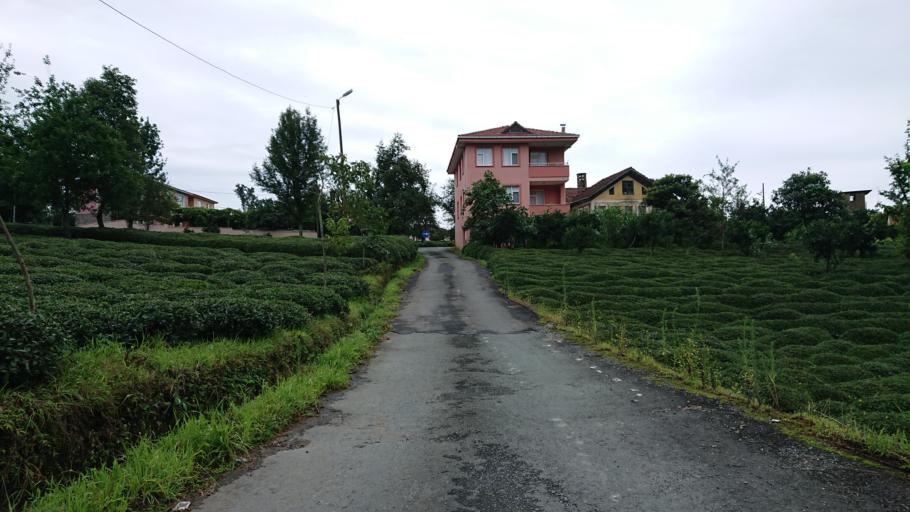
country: TR
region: Rize
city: Rize
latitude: 40.9832
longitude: 40.4851
